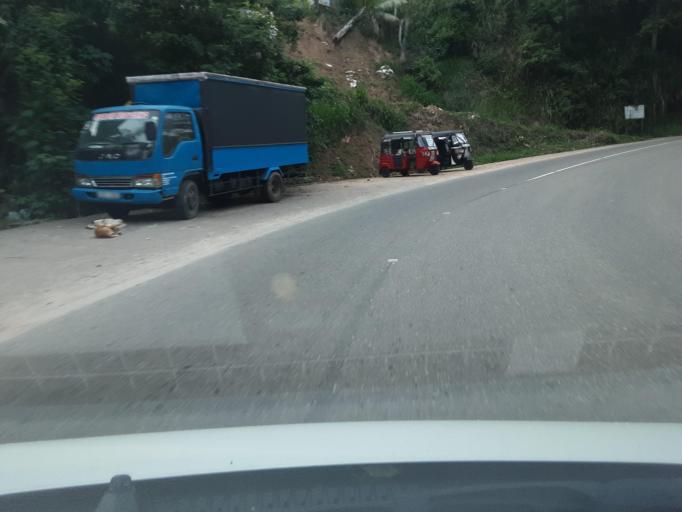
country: LK
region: Uva
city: Badulla
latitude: 6.9523
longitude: 81.0236
